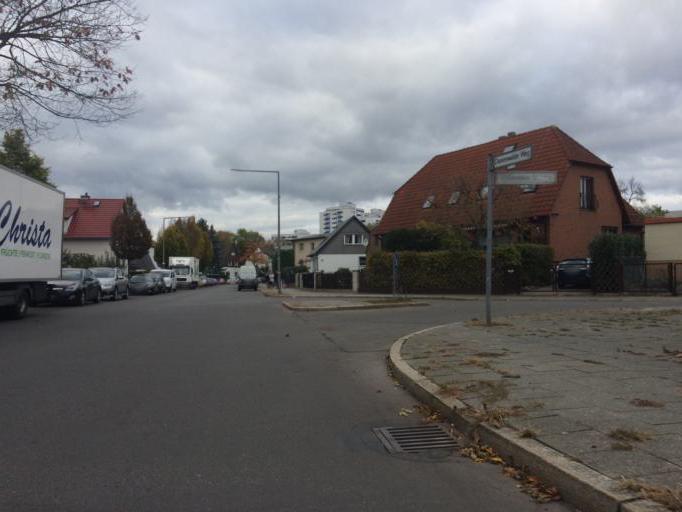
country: DE
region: Berlin
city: Markisches Viertel
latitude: 52.5941
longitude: 13.3412
